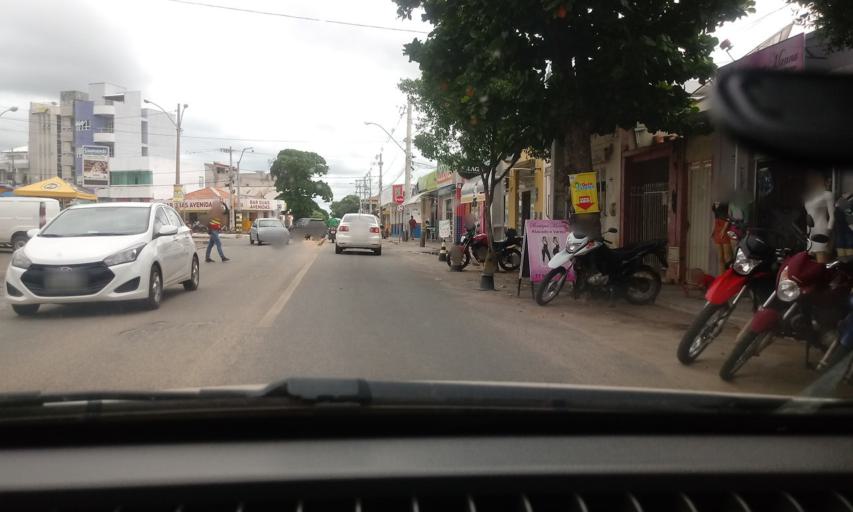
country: BR
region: Bahia
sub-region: Guanambi
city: Guanambi
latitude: -14.2200
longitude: -42.7797
